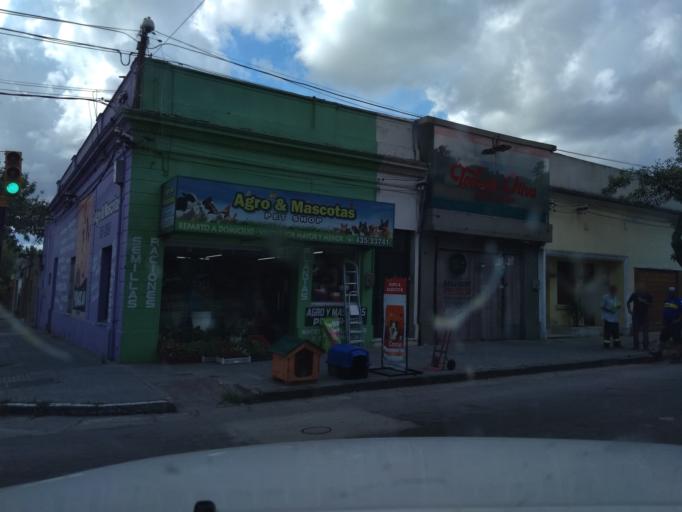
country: UY
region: Florida
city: Florida
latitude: -34.0937
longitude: -56.2192
